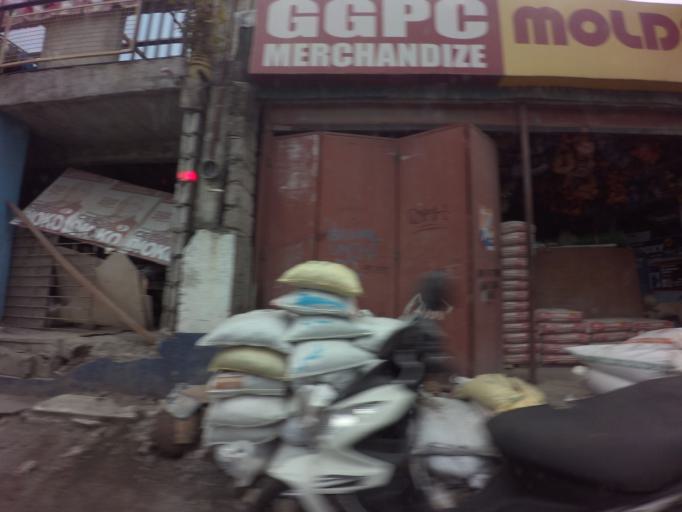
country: PH
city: Sambayanihan People's Village
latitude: 14.4317
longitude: 121.0500
